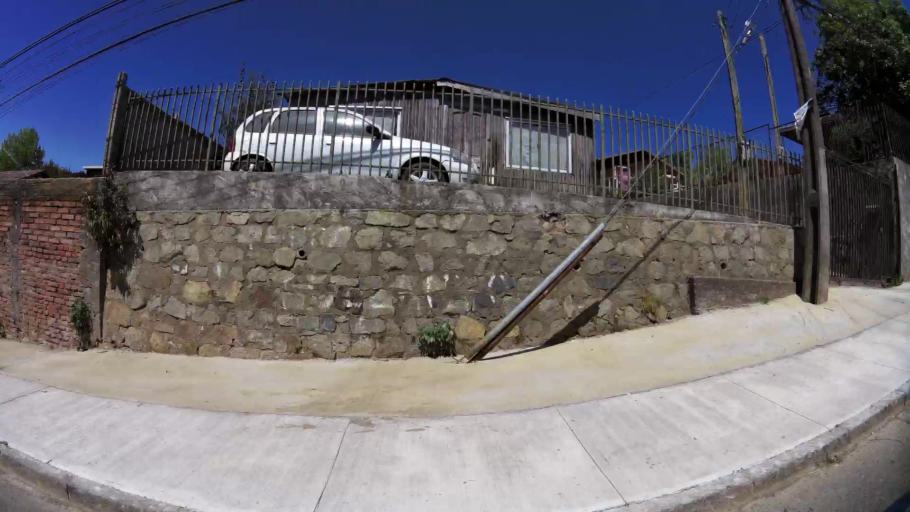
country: CL
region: Biobio
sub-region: Provincia de Concepcion
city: Penco
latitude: -36.7458
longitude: -72.9925
